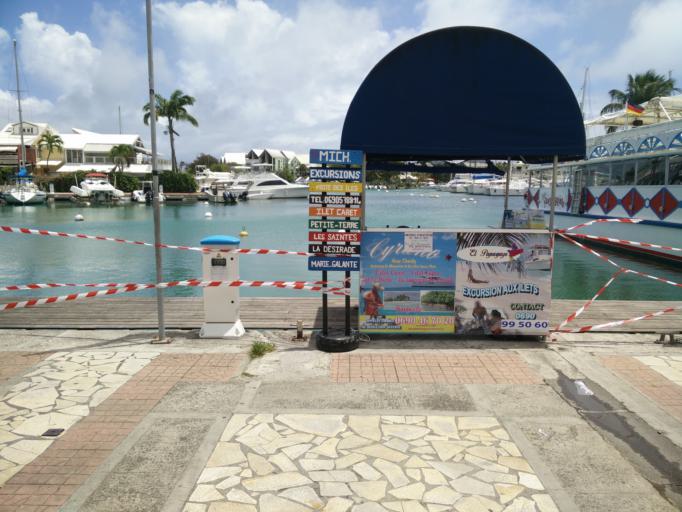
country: GP
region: Guadeloupe
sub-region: Guadeloupe
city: Pointe-a-Pitre
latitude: 16.2198
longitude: -61.5282
